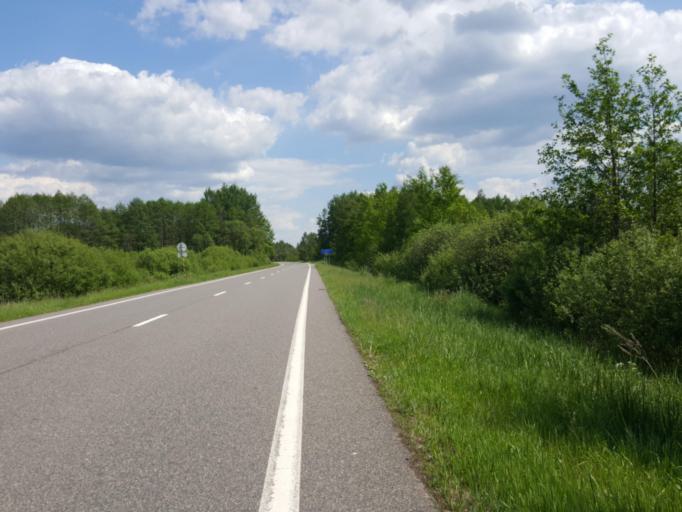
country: BY
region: Brest
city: Kamyanyuki
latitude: 52.5548
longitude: 23.6367
